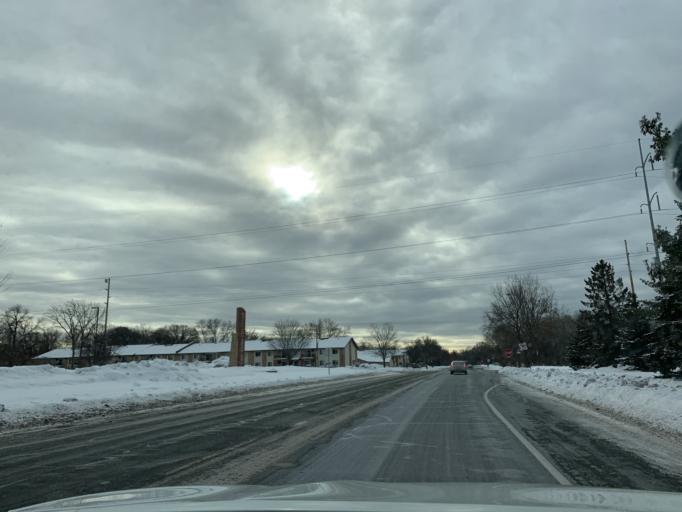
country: US
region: Minnesota
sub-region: Hennepin County
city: West Coon Rapids
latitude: 45.1726
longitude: -93.3044
